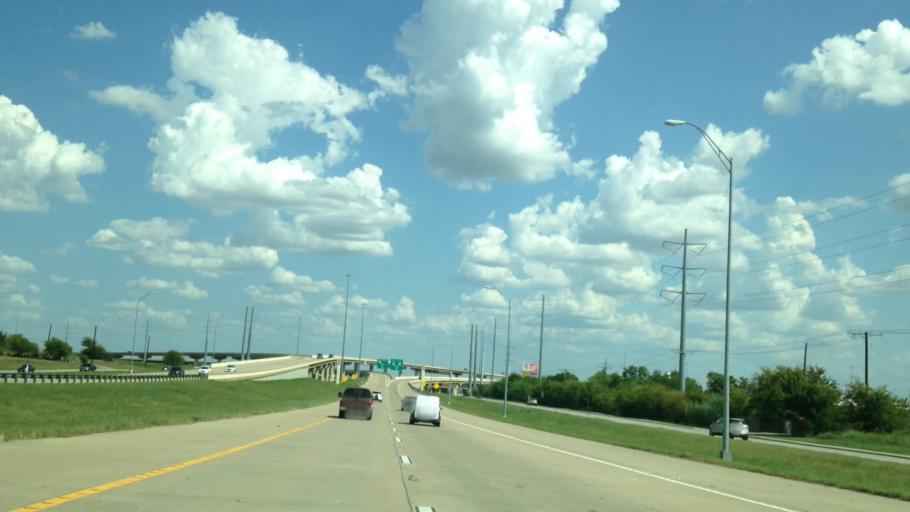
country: US
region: Texas
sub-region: Travis County
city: Pflugerville
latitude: 30.4773
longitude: -97.6003
